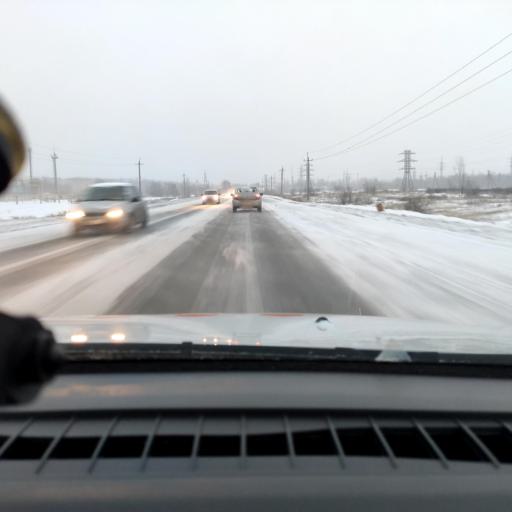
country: RU
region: Samara
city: Otradnyy
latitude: 53.3476
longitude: 51.3121
